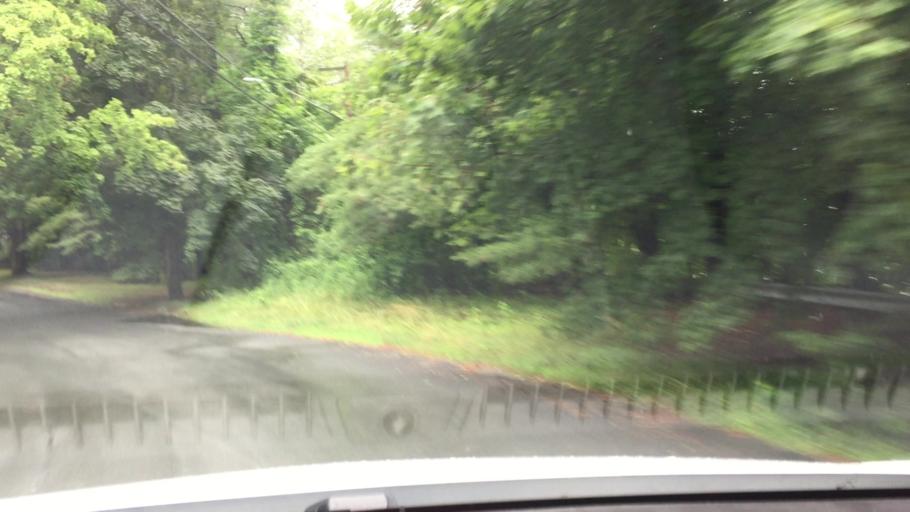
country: US
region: Massachusetts
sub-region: Berkshire County
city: Pittsfield
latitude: 42.4310
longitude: -73.2131
